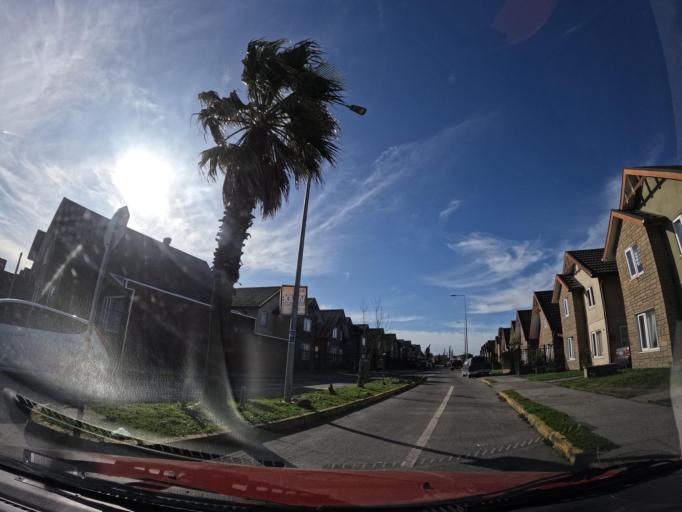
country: CL
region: Biobio
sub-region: Provincia de Concepcion
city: Concepcion
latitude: -36.7705
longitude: -73.0684
